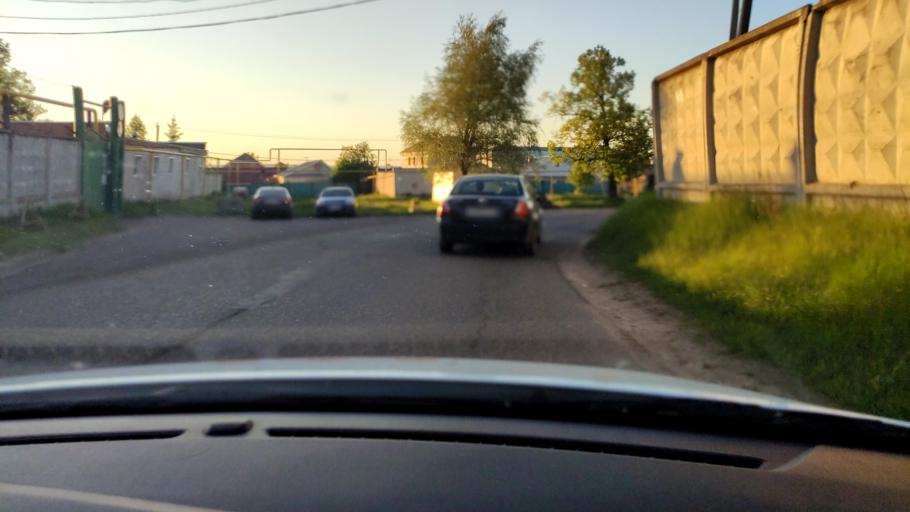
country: RU
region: Tatarstan
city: Vysokaya Gora
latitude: 55.9284
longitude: 49.3108
